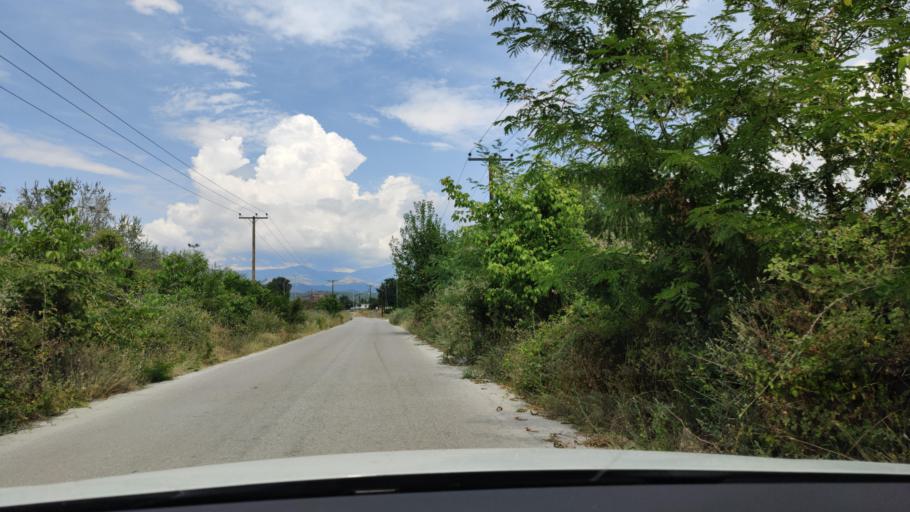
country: GR
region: Central Macedonia
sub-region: Nomos Serron
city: Serres
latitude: 41.0697
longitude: 23.5564
